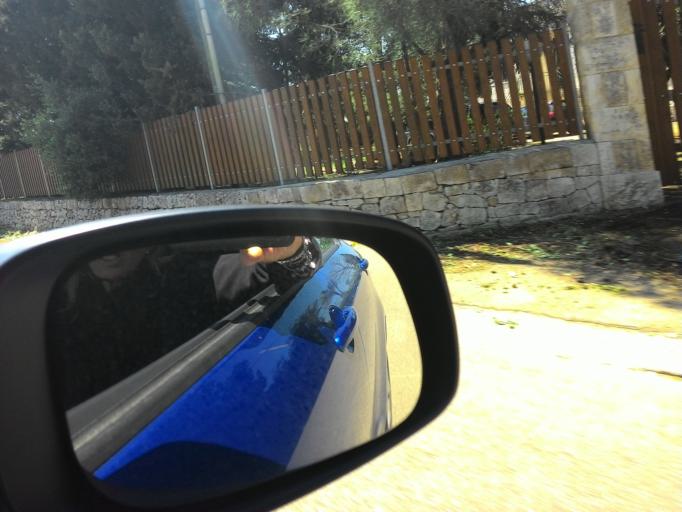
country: IT
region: Apulia
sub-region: Provincia di Bari
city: Putignano
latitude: 40.8481
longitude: 17.1429
